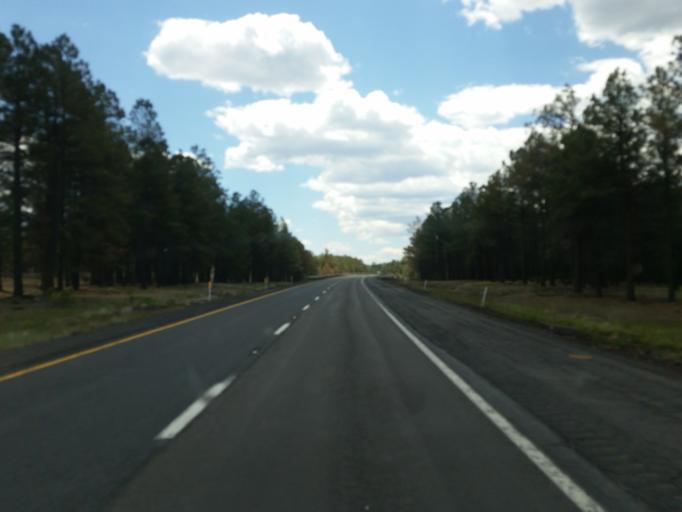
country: US
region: Arizona
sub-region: Coconino County
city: Flagstaff
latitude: 35.2212
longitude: -111.7929
